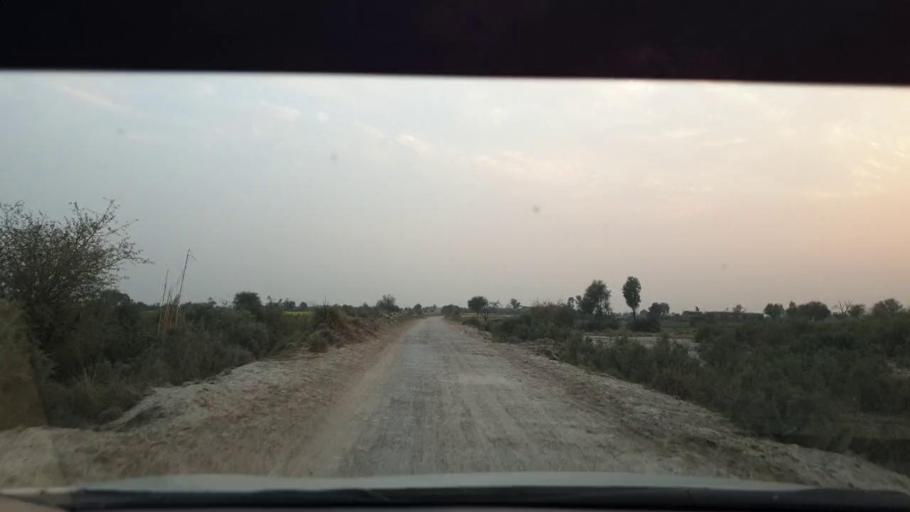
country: PK
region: Sindh
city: Berani
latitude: 25.8875
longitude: 68.7527
